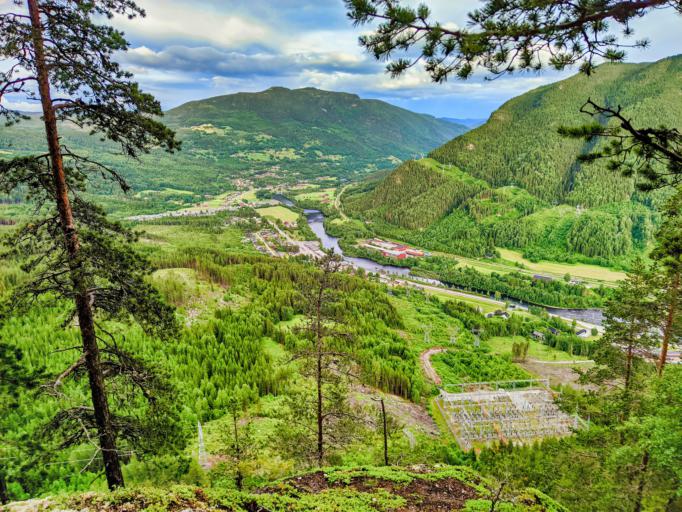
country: NO
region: Buskerud
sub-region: Gol
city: Gol
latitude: 60.7080
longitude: 8.9678
